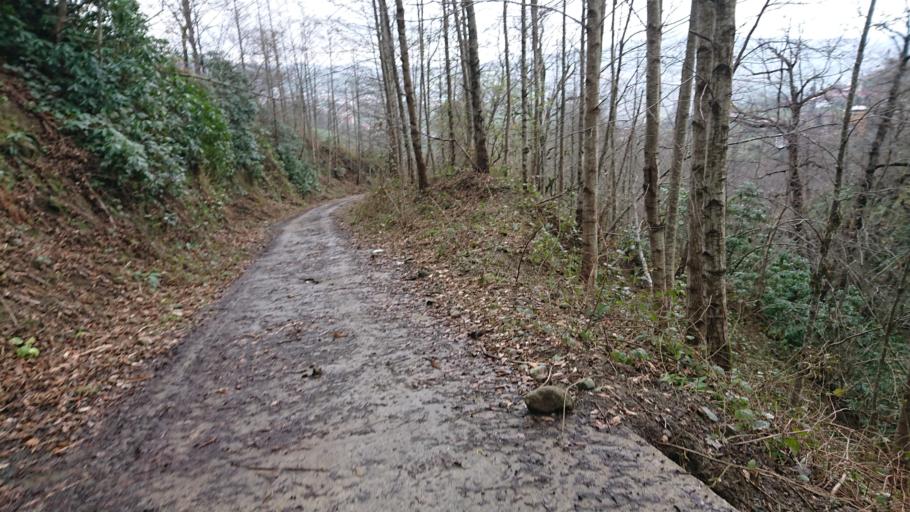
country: TR
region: Rize
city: Rize
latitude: 40.9782
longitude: 40.4970
